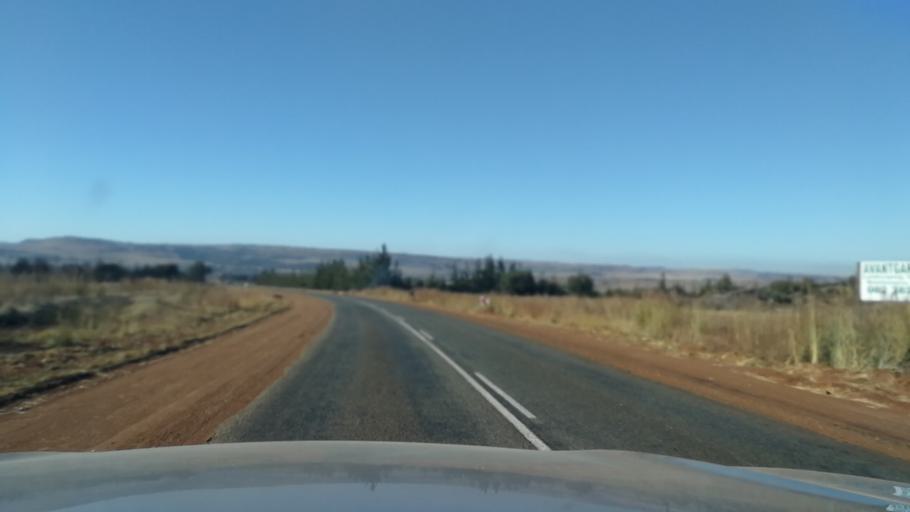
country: ZA
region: Gauteng
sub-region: West Rand District Municipality
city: Krugersdorp
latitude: -26.0003
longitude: 27.7019
